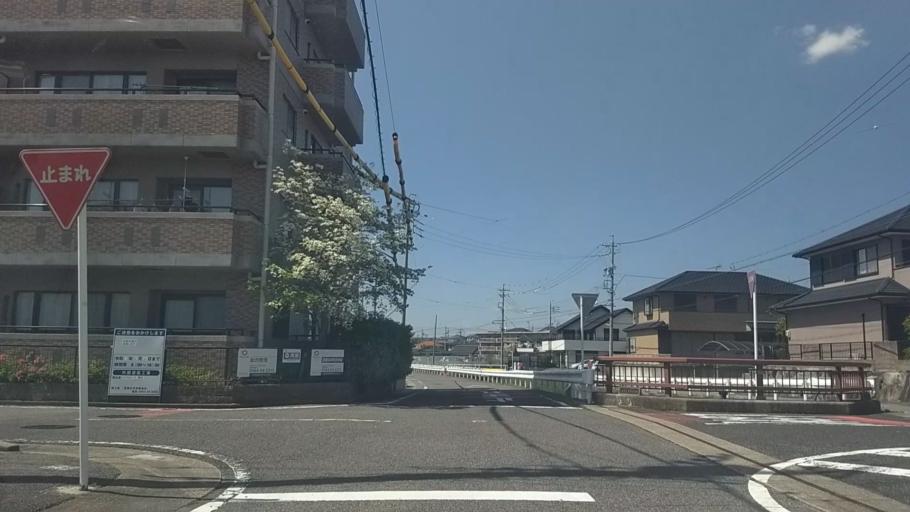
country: JP
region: Aichi
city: Okazaki
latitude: 34.9794
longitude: 137.1827
